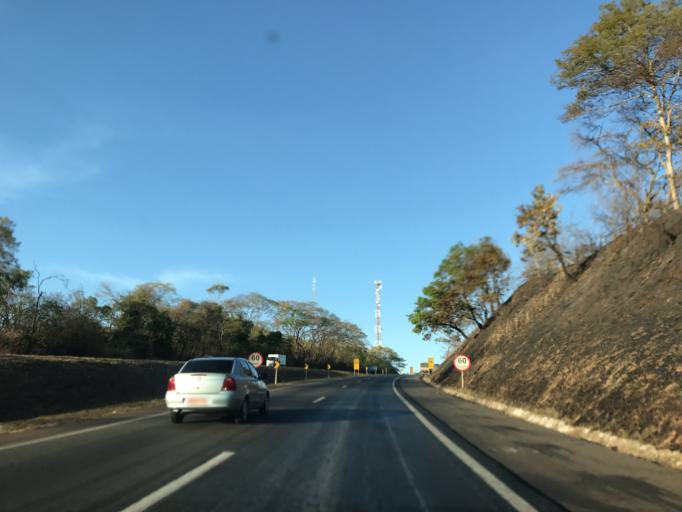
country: BR
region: Goias
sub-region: Goiania
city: Goiania
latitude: -16.5725
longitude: -49.1579
